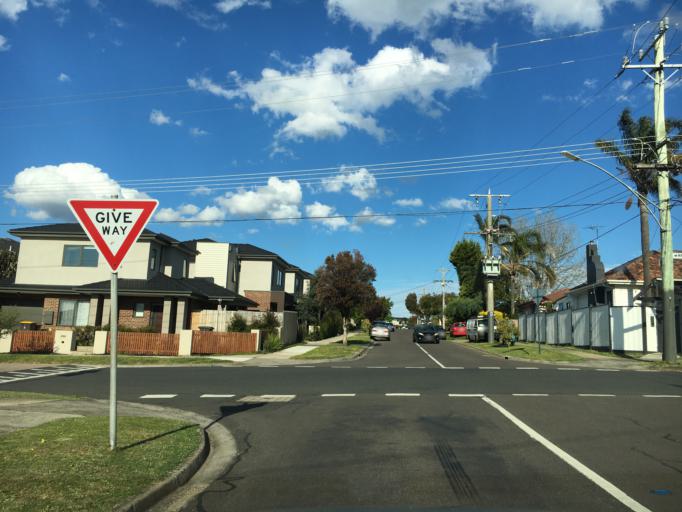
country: AU
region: Victoria
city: Clayton
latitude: -37.9004
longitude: 145.1141
